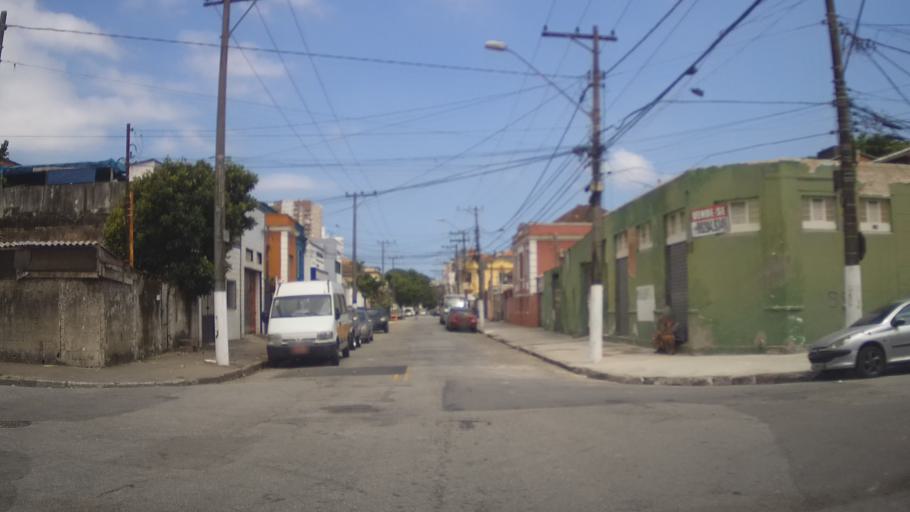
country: BR
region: Sao Paulo
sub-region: Santos
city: Santos
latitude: -23.9576
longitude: -46.3122
